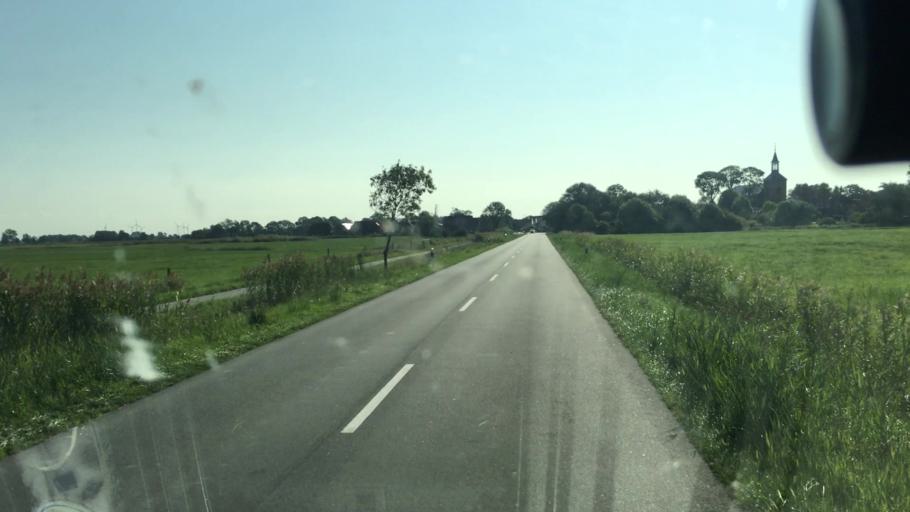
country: DE
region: Lower Saxony
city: Werdum
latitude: 53.6615
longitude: 7.7089
